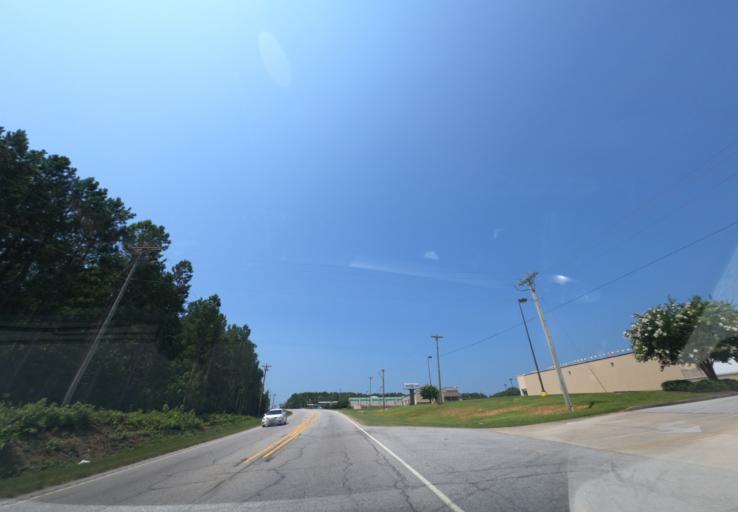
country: US
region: South Carolina
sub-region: Greenwood County
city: Greenwood
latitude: 34.1550
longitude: -82.1367
